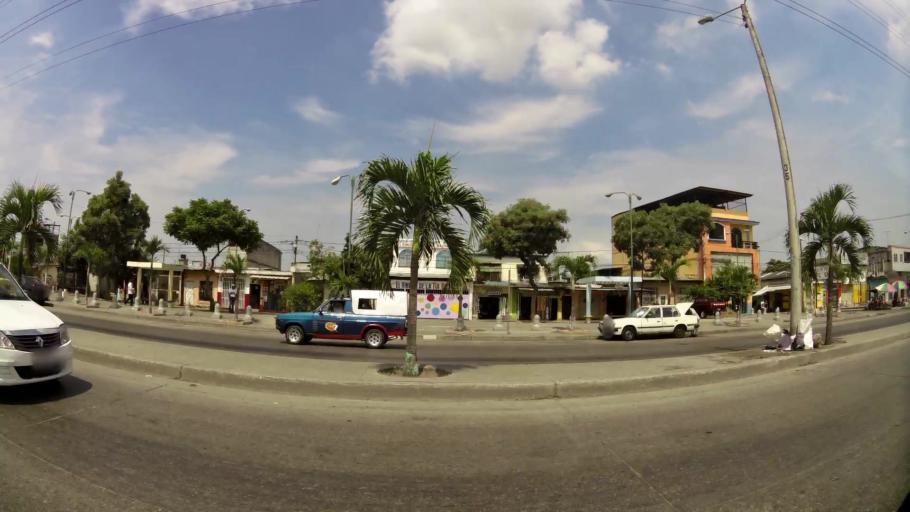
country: EC
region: Guayas
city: Guayaquil
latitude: -2.2599
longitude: -79.8836
